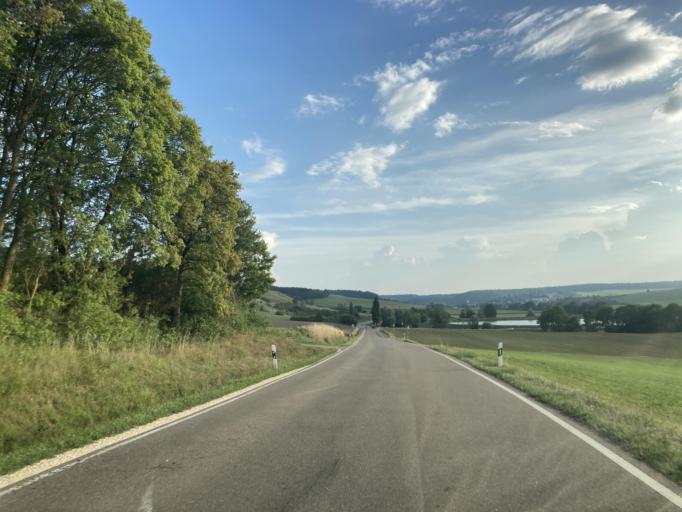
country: DE
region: Baden-Wuerttemberg
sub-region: Regierungsbezirk Stuttgart
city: Dischingen
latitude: 48.7190
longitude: 10.3834
